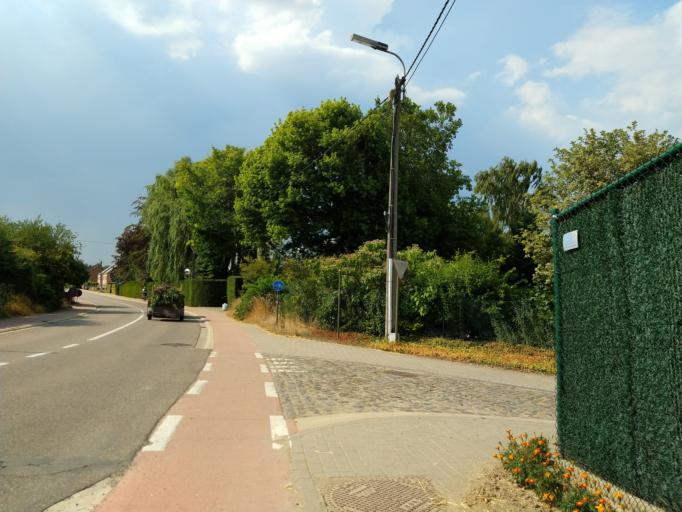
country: BE
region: Flanders
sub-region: Provincie Vlaams-Brabant
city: Bierbeek
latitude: 50.8300
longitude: 4.7529
